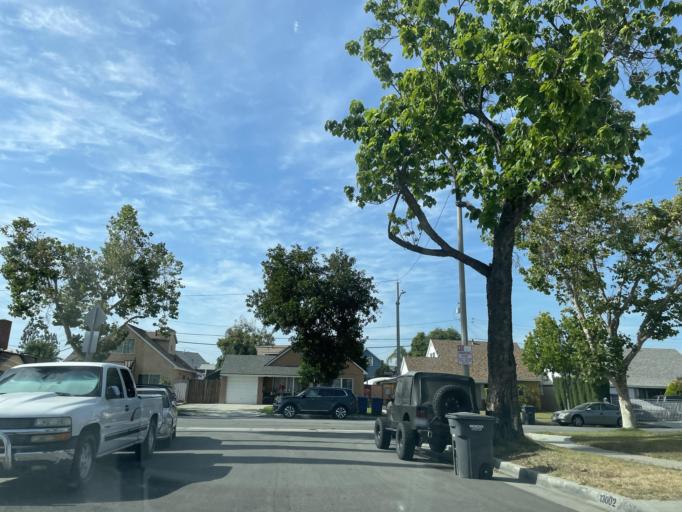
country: US
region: California
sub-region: Los Angeles County
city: La Mirada
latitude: 33.9128
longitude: -118.0374
